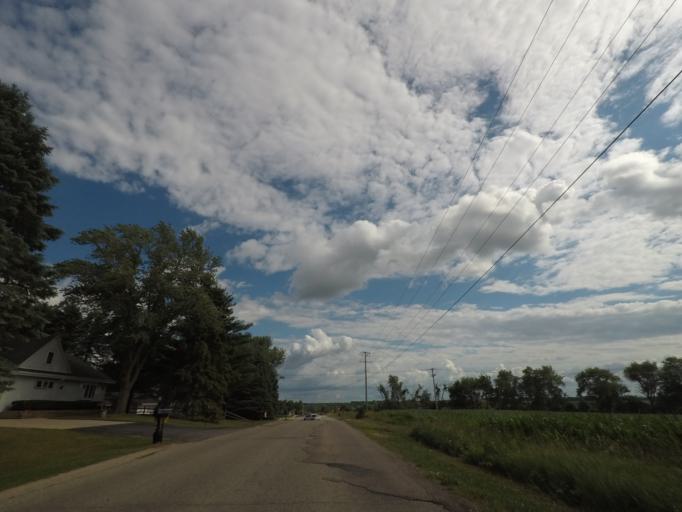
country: US
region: Wisconsin
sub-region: Rock County
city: Janesville
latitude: 42.6874
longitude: -89.0716
